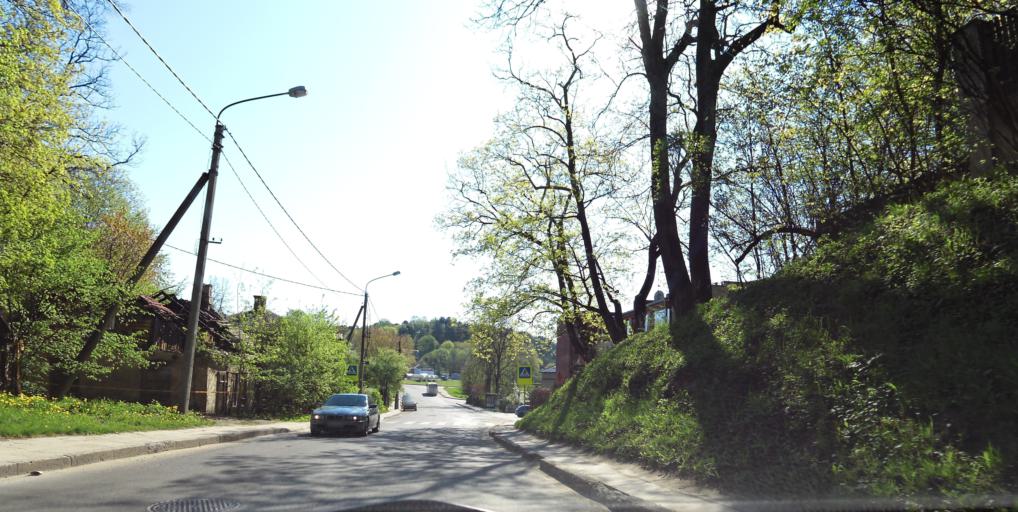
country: LT
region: Vilnius County
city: Rasos
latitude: 54.6822
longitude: 25.3106
